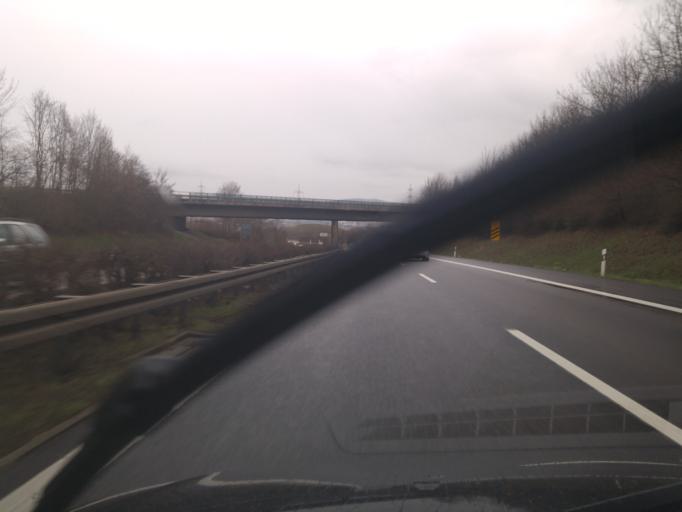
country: DE
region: Baden-Wuerttemberg
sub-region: Regierungsbezirk Stuttgart
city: Korb
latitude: 48.8485
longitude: 9.3474
